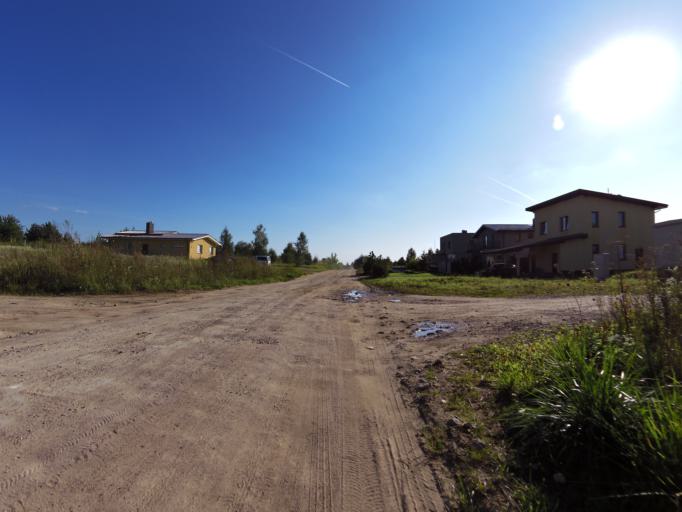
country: LT
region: Vilnius County
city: Pilaite
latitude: 54.7170
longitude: 25.1791
